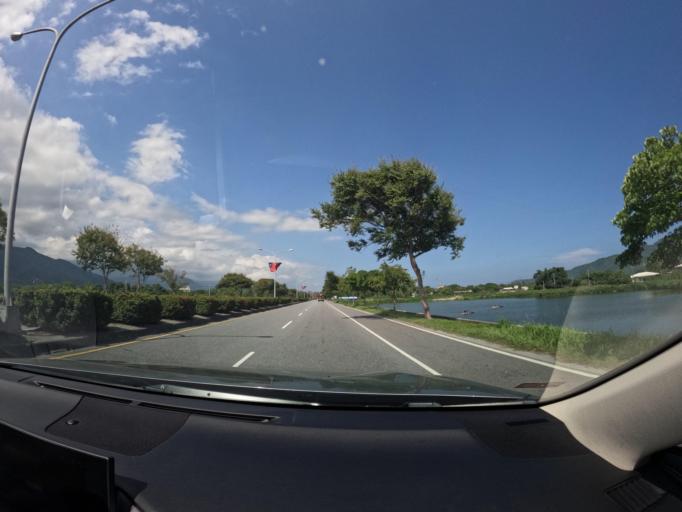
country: TW
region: Taiwan
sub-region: Hualien
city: Hualian
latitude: 23.8836
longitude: 121.5444
